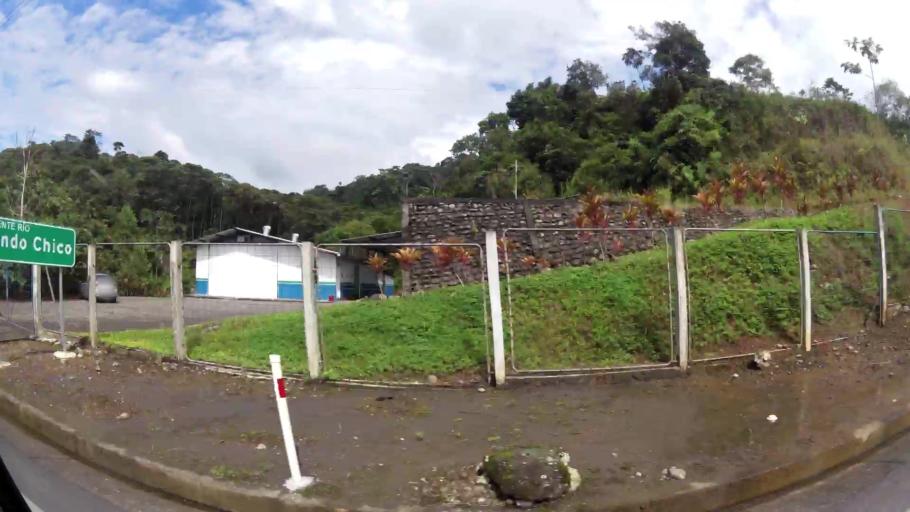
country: EC
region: Pastaza
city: Puyo
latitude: -1.4883
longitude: -78.0152
